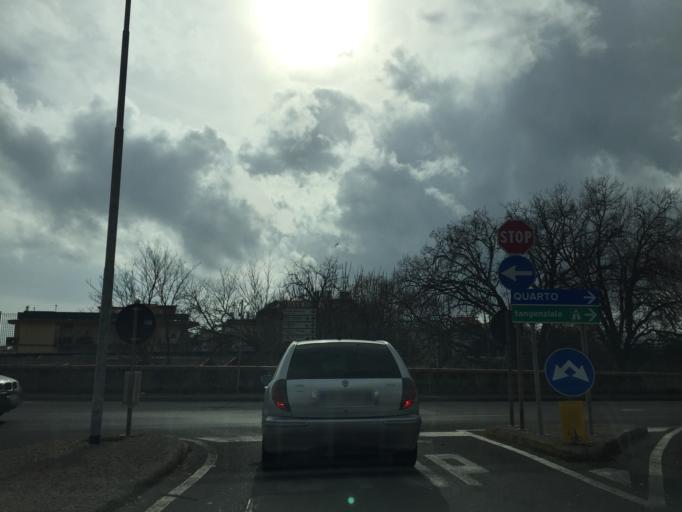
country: IT
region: Campania
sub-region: Provincia di Napoli
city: Pozzuoli
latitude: 40.8314
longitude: 14.1288
